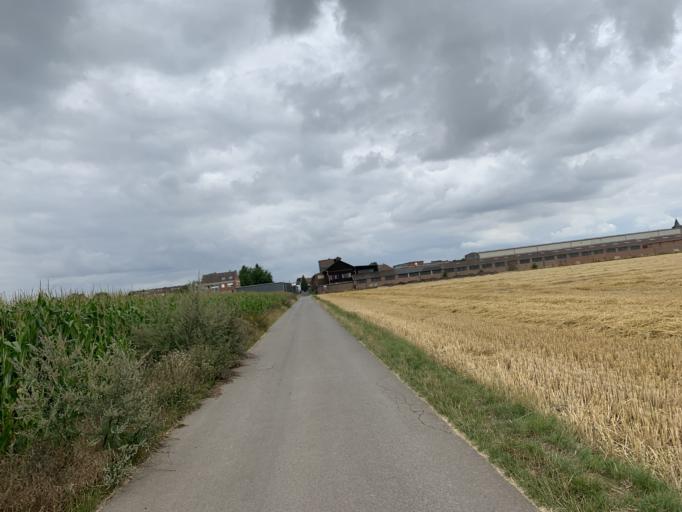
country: DE
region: North Rhine-Westphalia
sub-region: Regierungsbezirk Koln
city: Dueren
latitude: 50.8080
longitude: 6.5142
